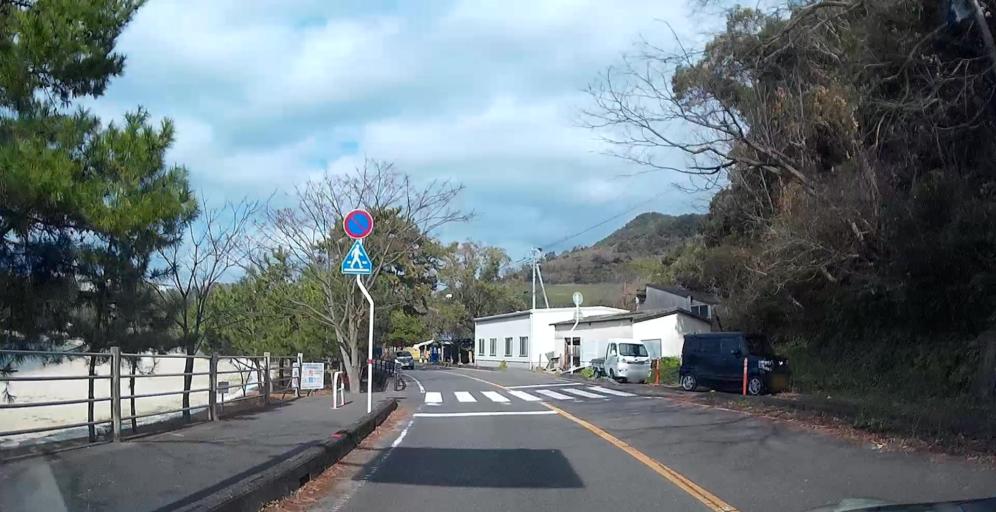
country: JP
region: Kumamoto
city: Minamata
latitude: 32.3167
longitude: 130.4719
